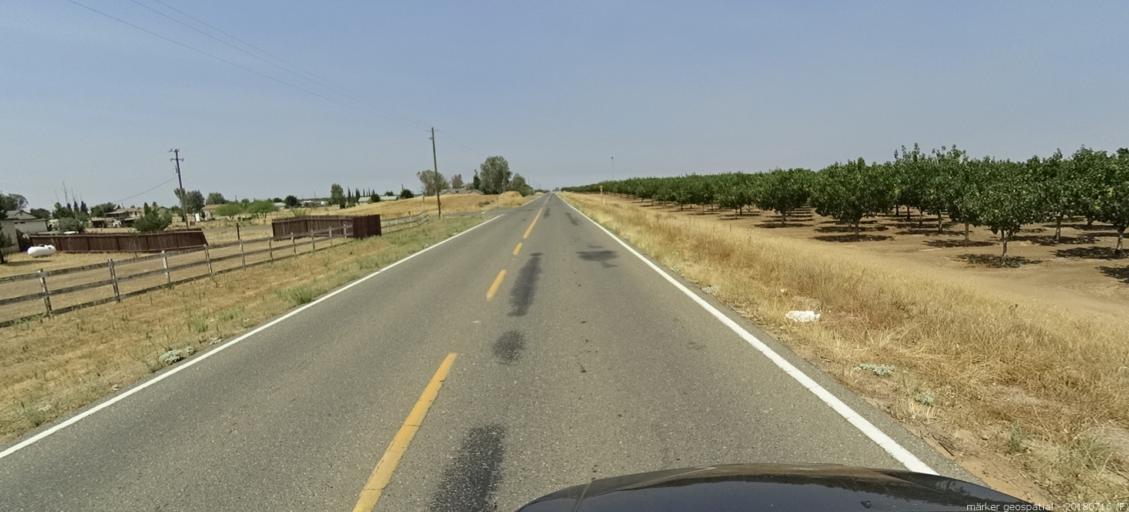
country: US
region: California
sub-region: Madera County
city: Madera Acres
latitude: 37.0540
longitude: -119.9950
